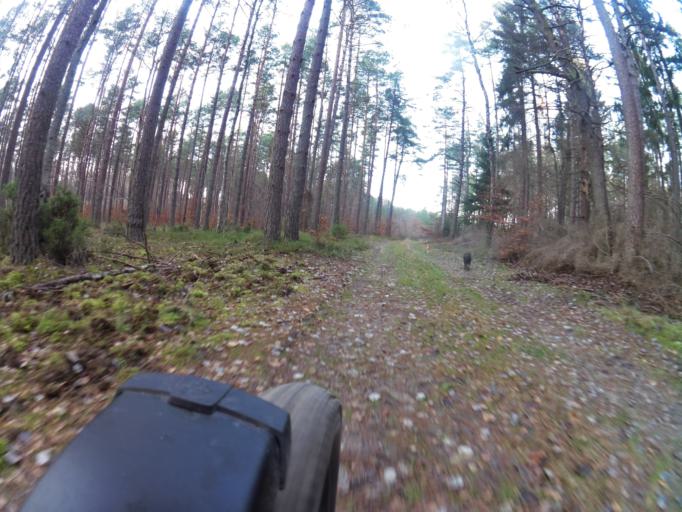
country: PL
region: West Pomeranian Voivodeship
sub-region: Powiat koszalinski
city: Polanow
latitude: 54.1476
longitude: 16.7105
